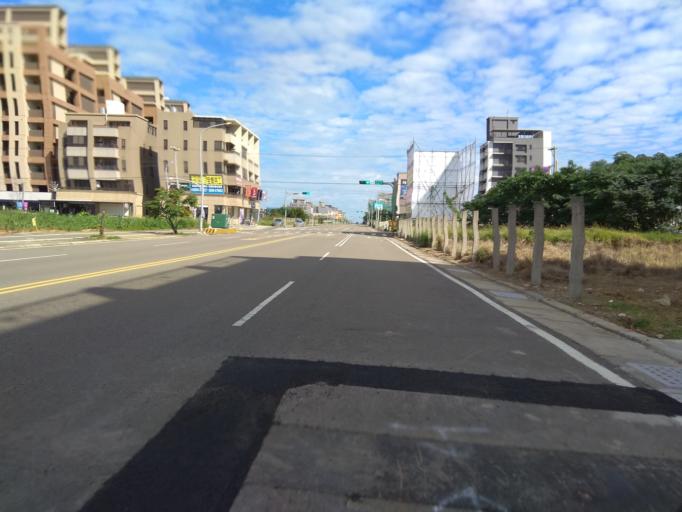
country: TW
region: Taiwan
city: Taoyuan City
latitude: 25.0445
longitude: 121.1348
